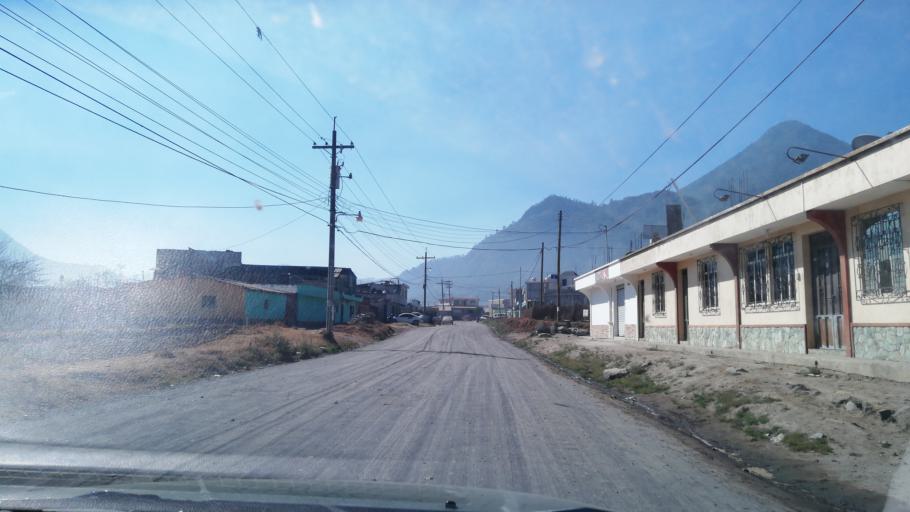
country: GT
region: Quetzaltenango
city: Quetzaltenango
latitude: 14.7994
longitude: -91.5499
